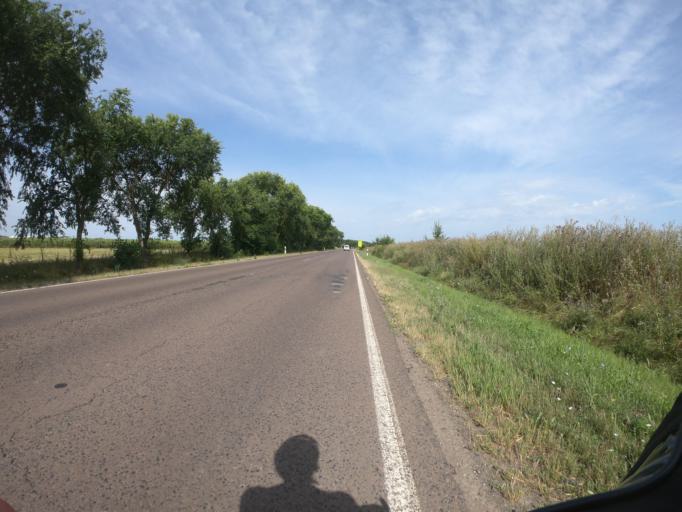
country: HU
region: Jasz-Nagykun-Szolnok
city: Tiszafured
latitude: 47.5963
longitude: 20.8257
